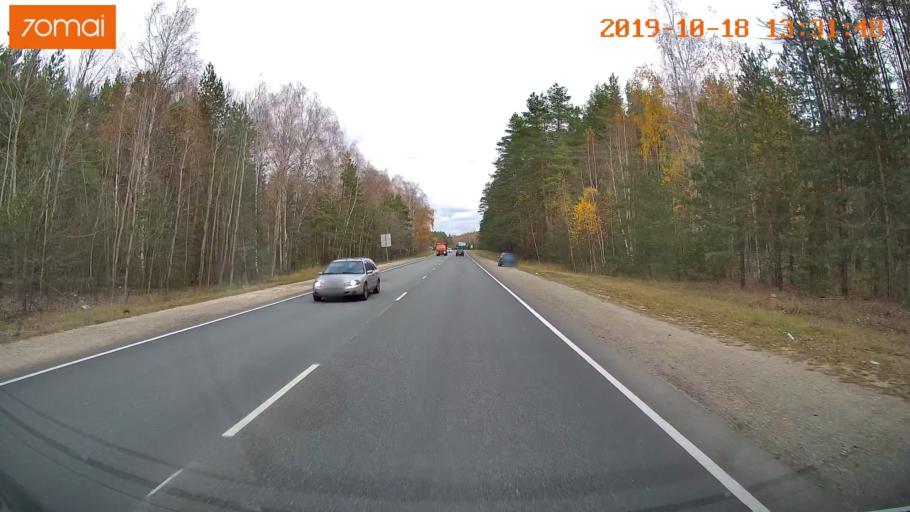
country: RU
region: Rjazan
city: Solotcha
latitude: 54.8256
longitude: 39.9074
